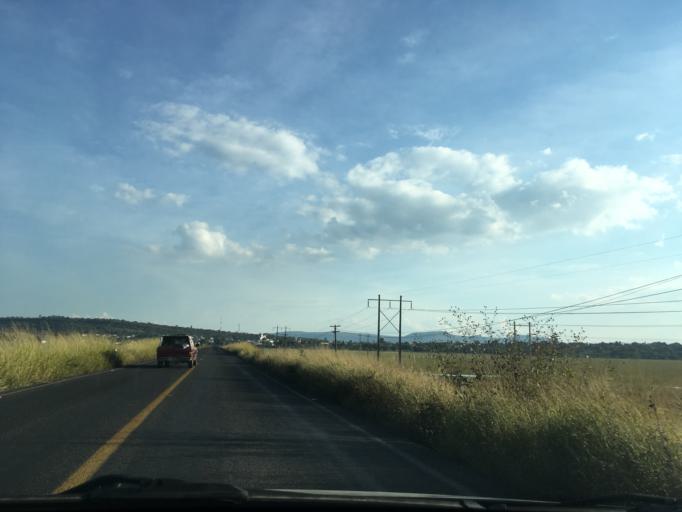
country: MX
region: Michoacan
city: Cuitzeo del Porvenir
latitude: 19.9852
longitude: -101.1474
